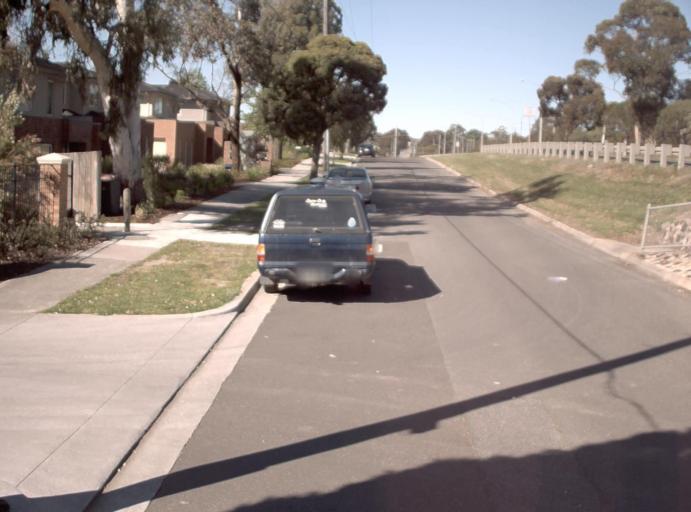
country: AU
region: Victoria
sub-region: Maroondah
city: Croydon North
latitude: -37.7815
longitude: 145.2865
